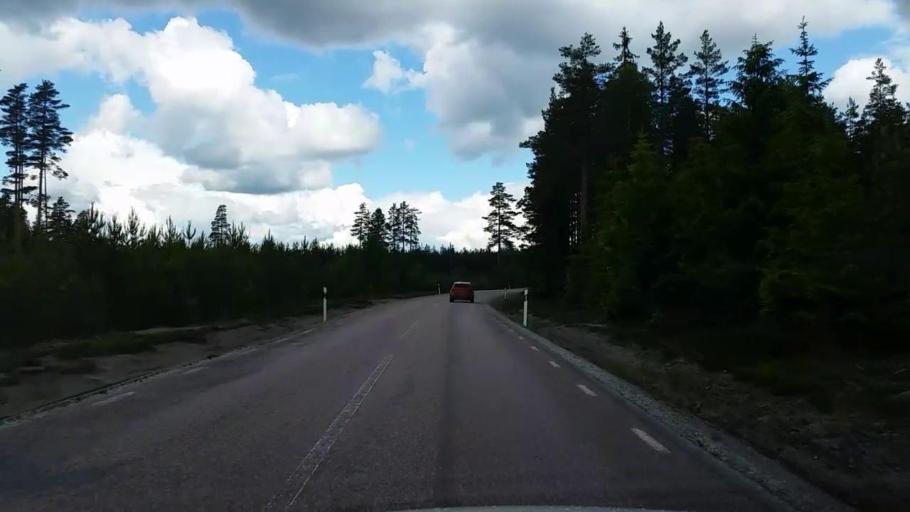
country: SE
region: Vaestmanland
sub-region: Fagersta Kommun
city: Fagersta
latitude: 59.8937
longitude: 15.8220
